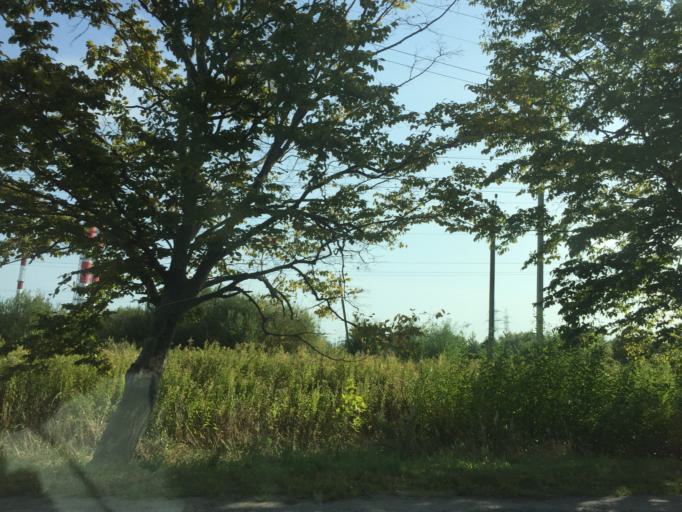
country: RU
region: Kaliningrad
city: Bol'shoe Isakovo
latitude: 54.6649
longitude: 20.5751
